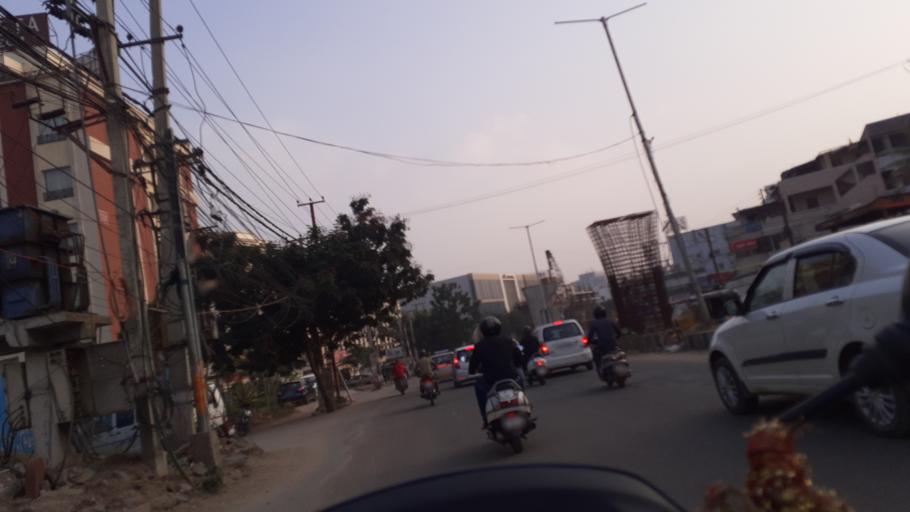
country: IN
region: Telangana
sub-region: Rangareddi
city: Kukatpalli
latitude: 17.4671
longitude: 78.3672
